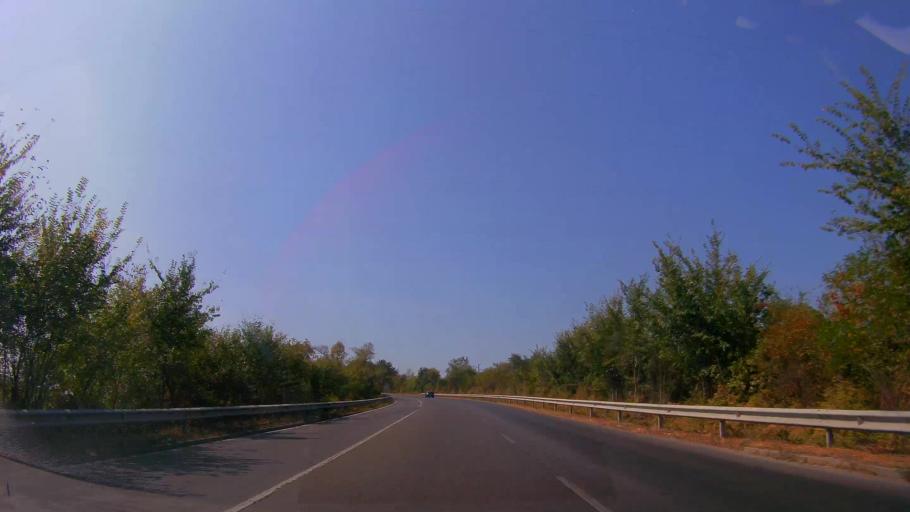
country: BG
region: Ruse
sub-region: Obshtina Vetovo
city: Senovo
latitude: 43.5613
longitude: 26.3798
